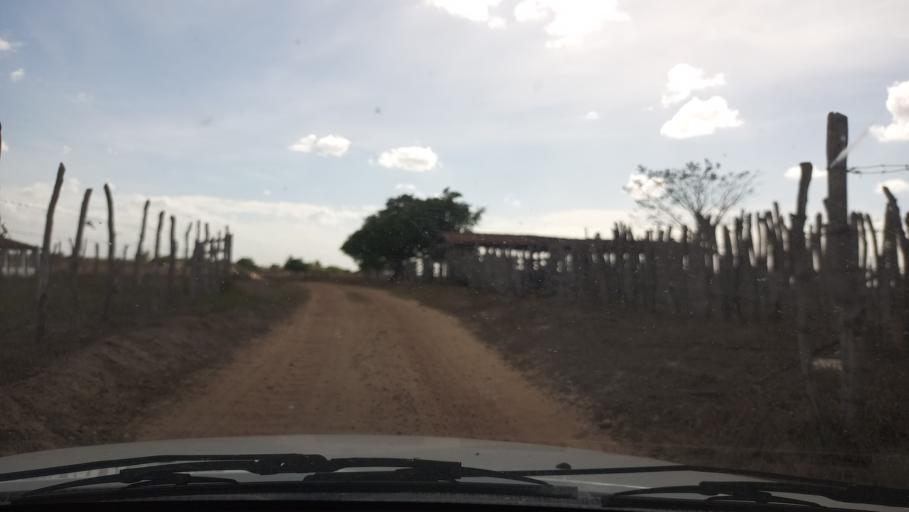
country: BR
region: Rio Grande do Norte
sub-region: Goianinha
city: Goianinha
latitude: -6.3064
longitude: -35.3050
